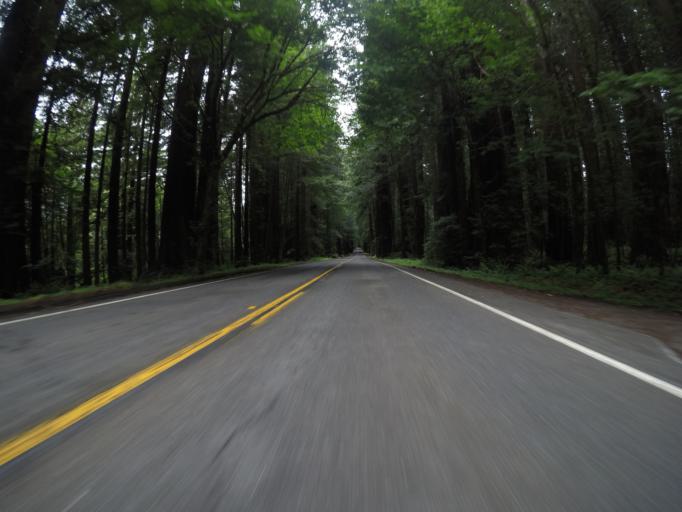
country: US
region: California
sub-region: Humboldt County
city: Rio Dell
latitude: 40.4427
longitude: -124.0255
